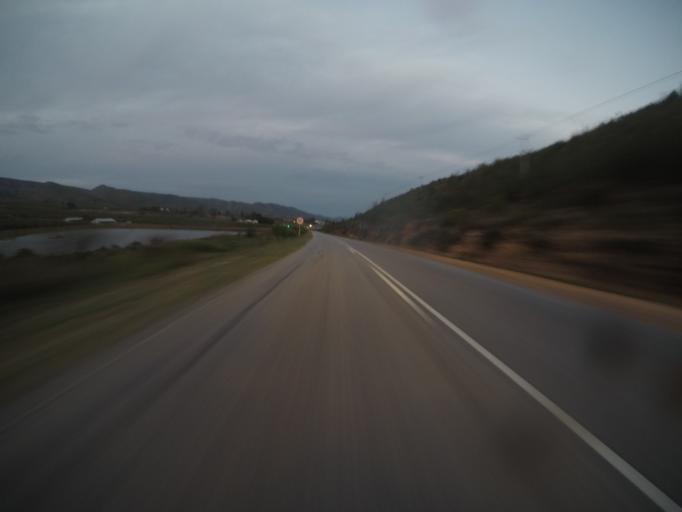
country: ZA
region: Western Cape
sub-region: Eden District Municipality
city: Plettenberg Bay
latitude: -33.8122
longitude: 23.7212
